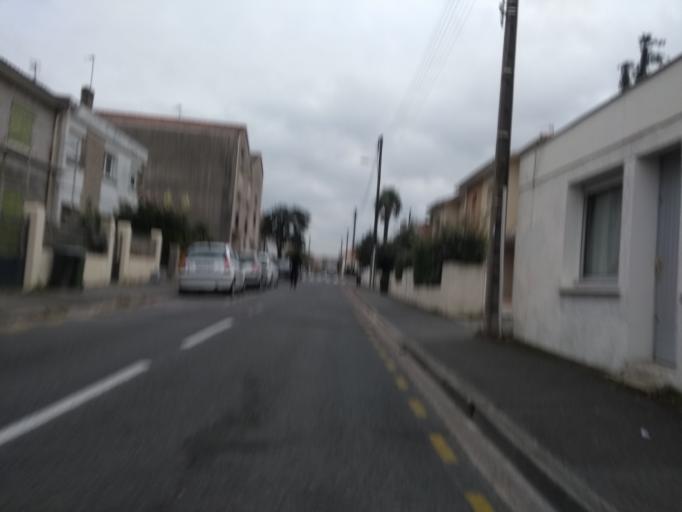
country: FR
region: Aquitaine
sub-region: Departement de la Gironde
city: Talence
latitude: 44.8040
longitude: -0.5955
